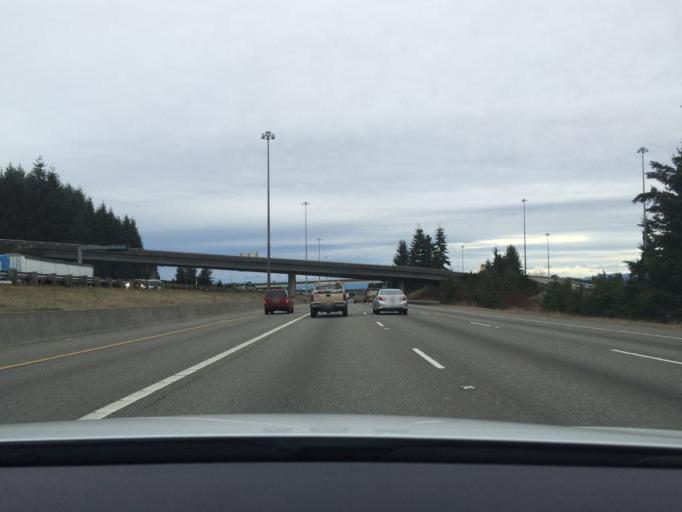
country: US
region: Washington
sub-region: Snohomish County
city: Mill Creek
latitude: 47.9137
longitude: -122.2087
